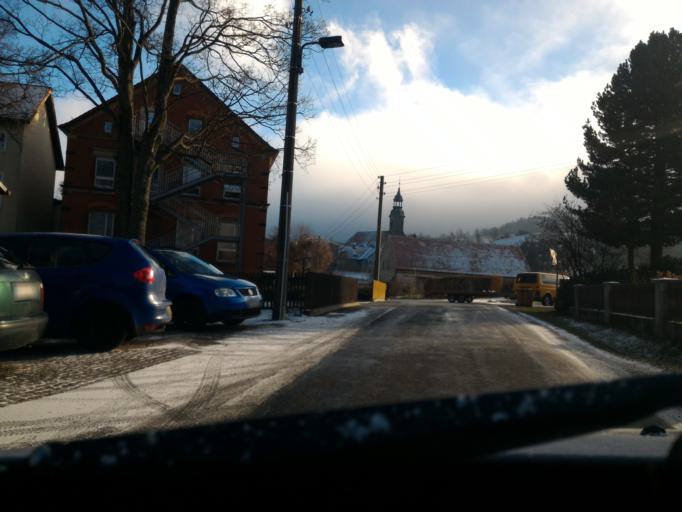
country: DE
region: Saxony
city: Grossschonau
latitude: 50.8709
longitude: 14.6479
